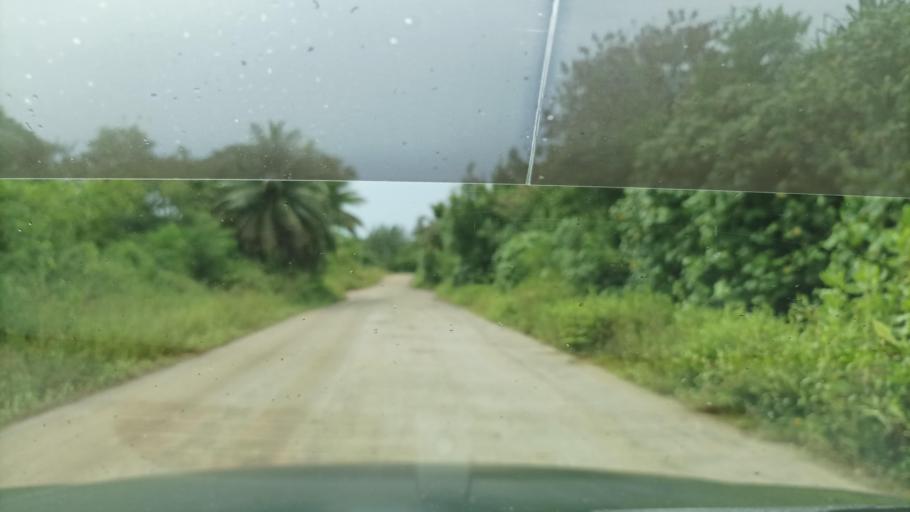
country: FM
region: Yap
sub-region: Weloy Municipality
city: Colonia
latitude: 9.5417
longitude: 138.1680
